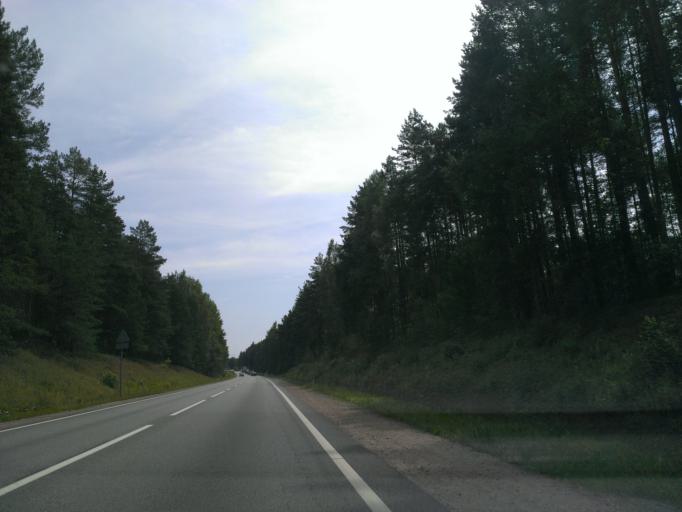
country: LV
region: Riga
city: Bergi
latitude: 56.9840
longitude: 24.3233
